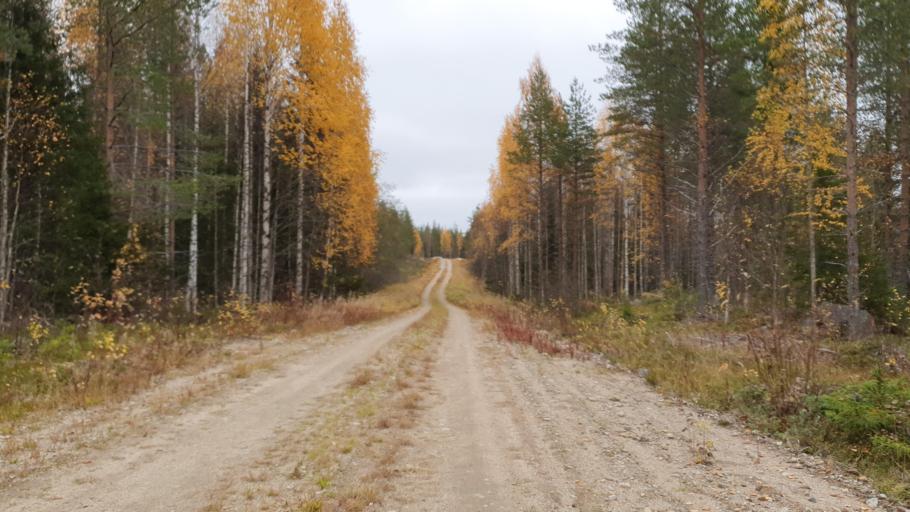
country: FI
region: Kainuu
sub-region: Kehys-Kainuu
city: Kuhmo
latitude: 64.4393
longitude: 29.6294
